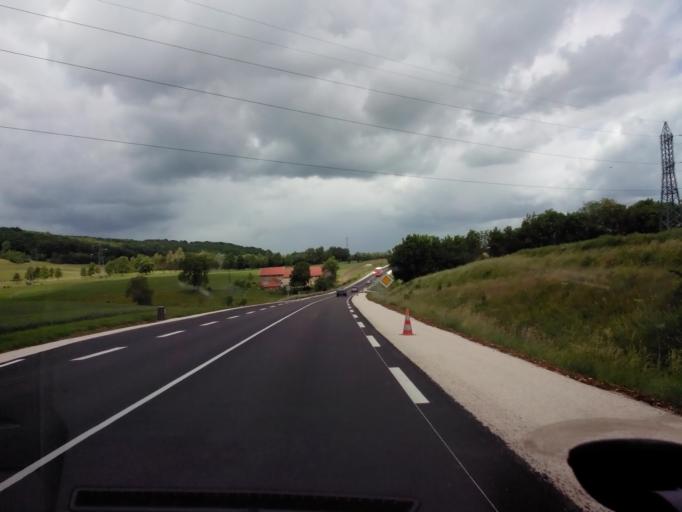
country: FR
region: Champagne-Ardenne
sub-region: Departement de la Haute-Marne
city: Rolampont
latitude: 47.9253
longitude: 5.2909
